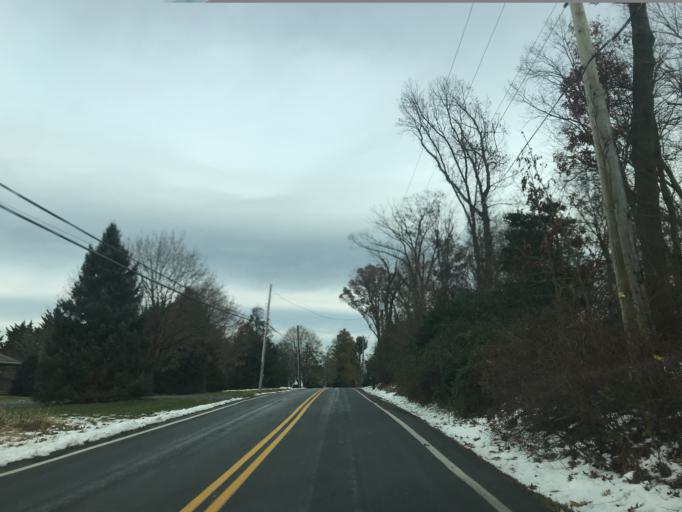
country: US
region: Pennsylvania
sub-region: York County
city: Susquehanna Trails
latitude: 39.6924
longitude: -76.3963
